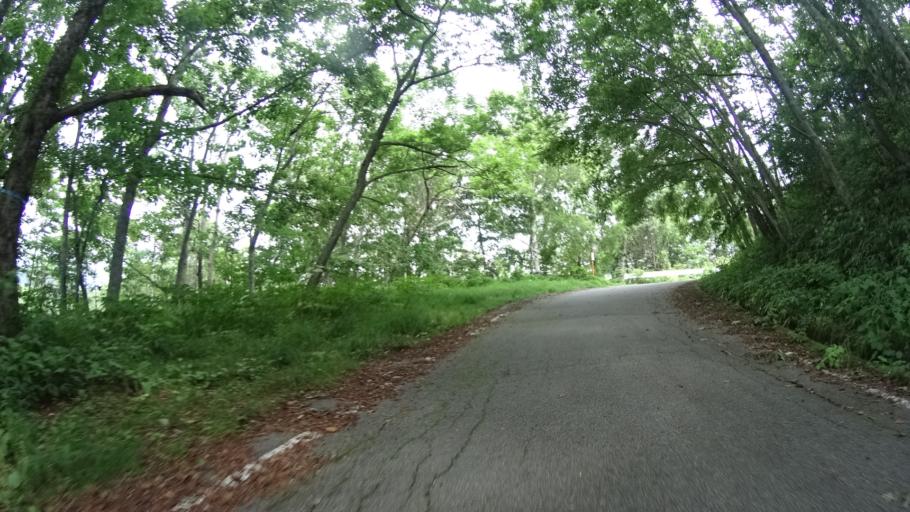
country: JP
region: Yamanashi
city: Enzan
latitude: 35.8049
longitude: 138.6355
